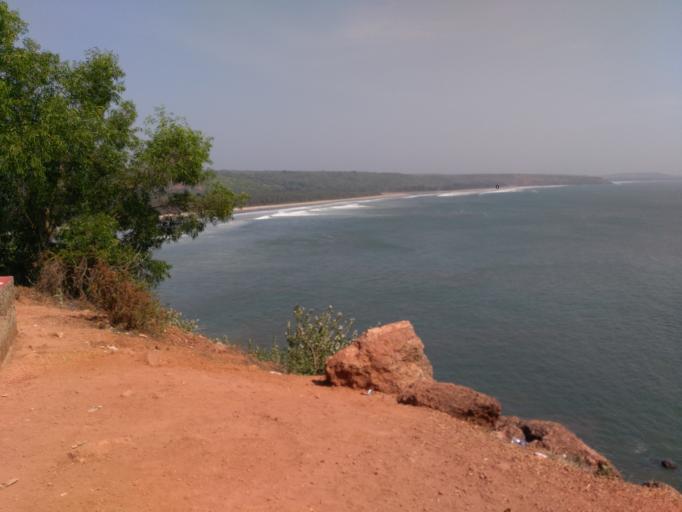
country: IN
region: Maharashtra
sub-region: Ratnagiri
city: Ratnagiri
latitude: 17.1139
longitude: 73.2733
